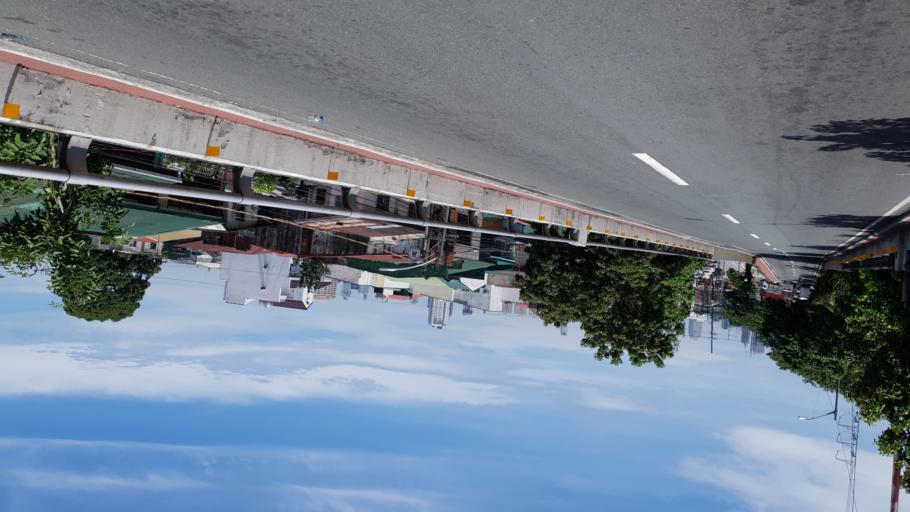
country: PH
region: Metro Manila
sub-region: City of Manila
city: Quiapo
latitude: 14.5879
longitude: 121.0066
